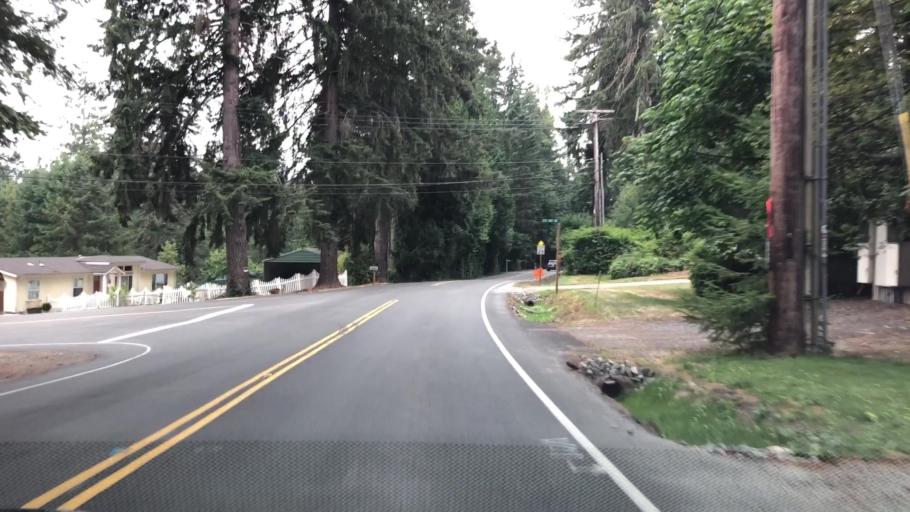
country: US
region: Washington
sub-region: King County
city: Cottage Lake
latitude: 47.7495
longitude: -122.1081
